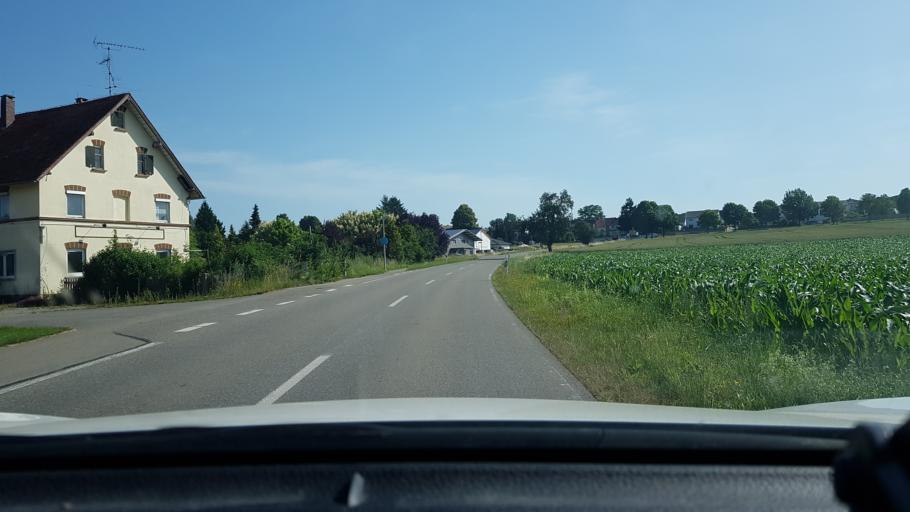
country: DE
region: Baden-Wuerttemberg
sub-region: Tuebingen Region
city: Schwendi
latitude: 48.2051
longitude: 9.9602
